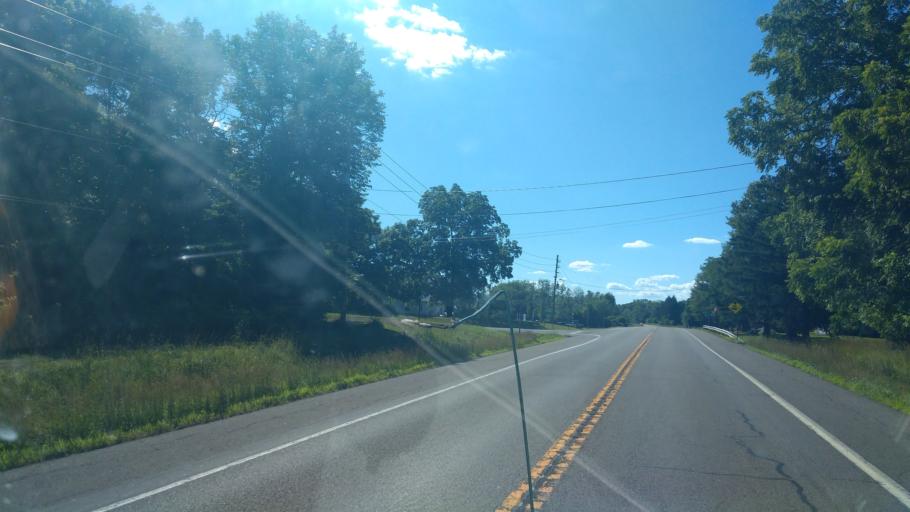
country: US
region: New York
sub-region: Seneca County
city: Seneca Falls
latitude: 42.9566
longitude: -76.8187
